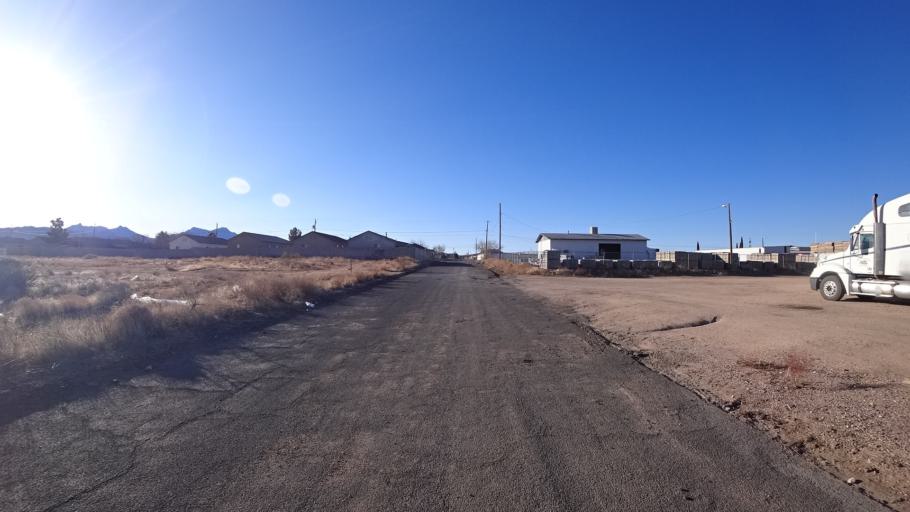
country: US
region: Arizona
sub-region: Mohave County
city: Kingman
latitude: 35.2071
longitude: -114.0158
